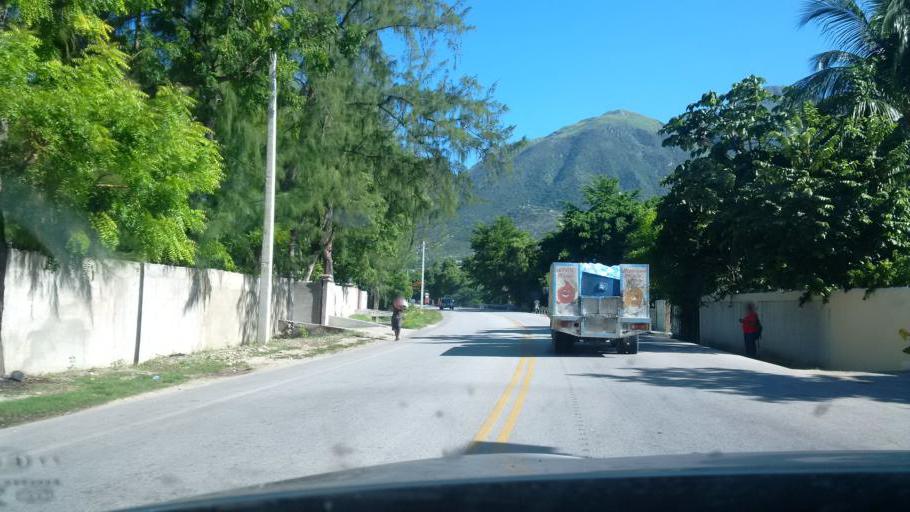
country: HT
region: Artibonite
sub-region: Arrondissement de Saint-Marc
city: Verrettes
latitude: 18.8815
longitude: -72.6157
